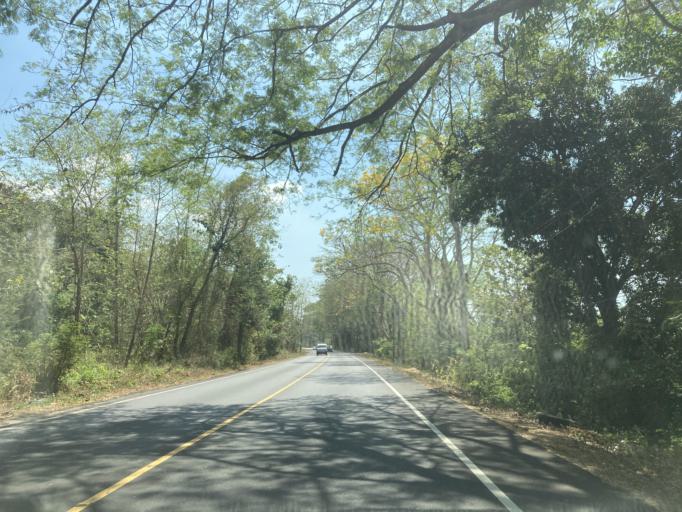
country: GT
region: Escuintla
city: Guanagazapa
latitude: 14.1796
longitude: -90.6876
